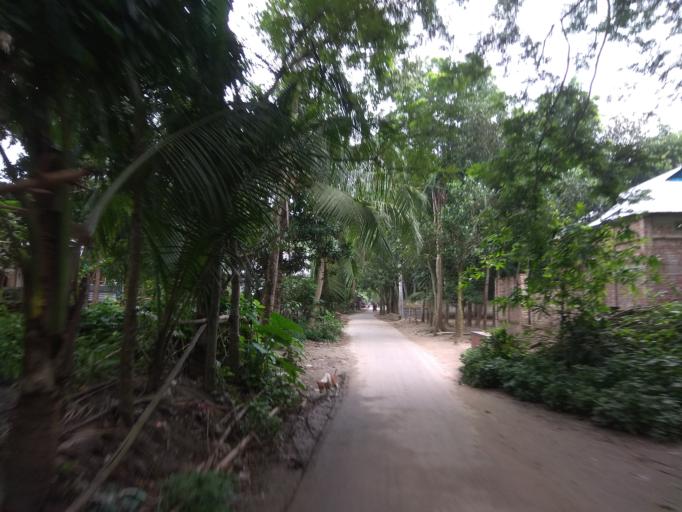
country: BD
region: Dhaka
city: Dohar
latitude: 23.4840
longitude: 90.0052
